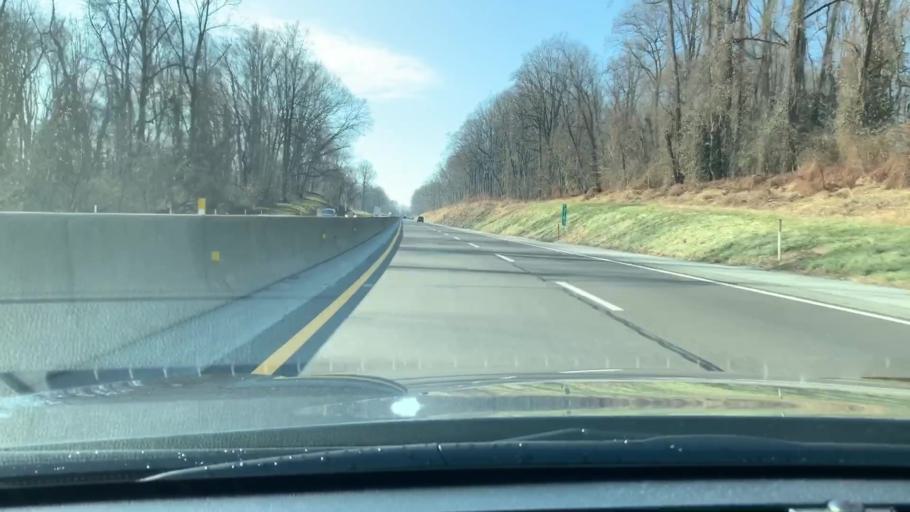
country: US
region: Pennsylvania
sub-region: Chester County
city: Malvern
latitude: 40.0769
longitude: -75.5485
